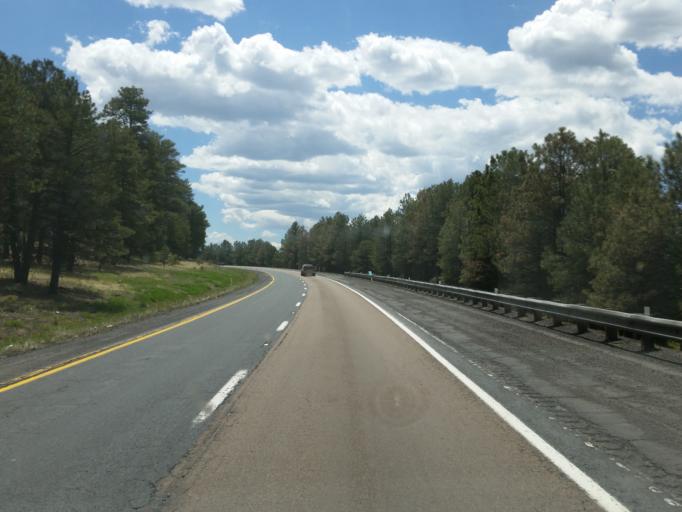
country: US
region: Arizona
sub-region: Coconino County
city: Flagstaff
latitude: 35.2055
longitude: -111.7696
